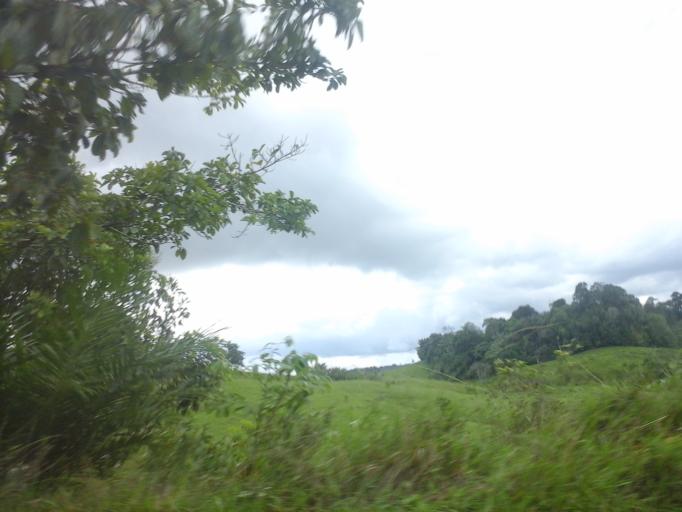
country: CO
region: Caqueta
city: El Doncello
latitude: 1.6319
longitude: -75.1402
